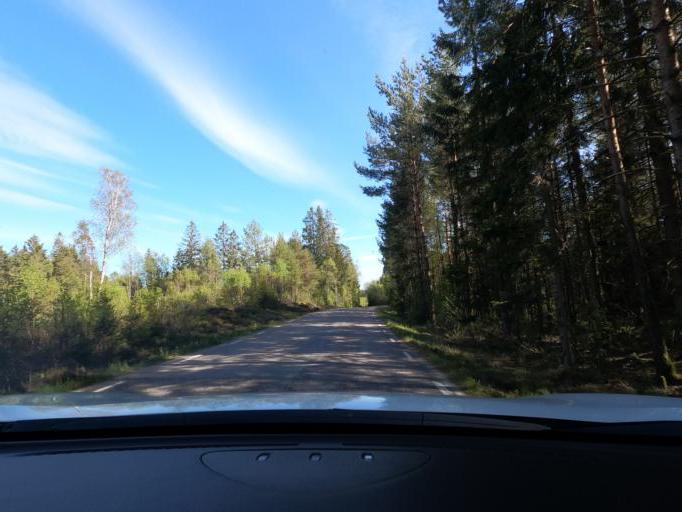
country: SE
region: Vaestra Goetaland
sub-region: Harryda Kommun
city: Hindas
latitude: 57.6630
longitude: 12.3530
